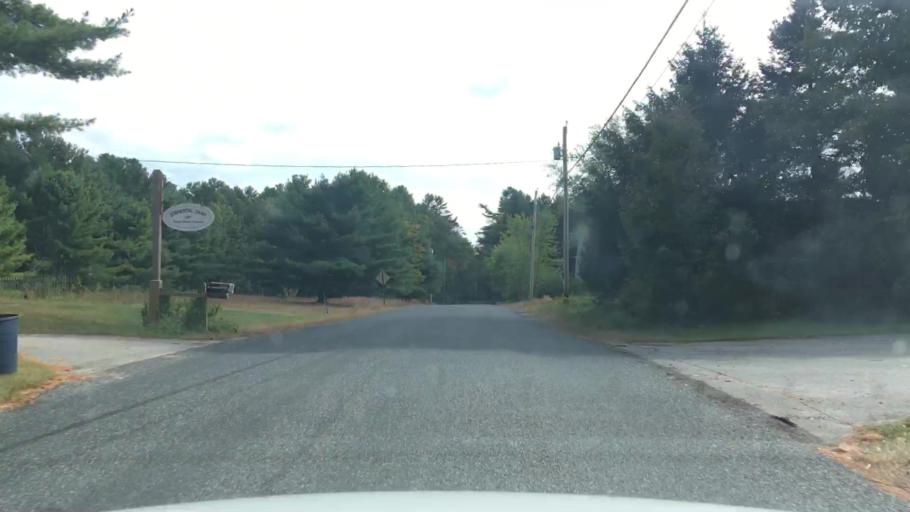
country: US
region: Maine
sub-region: Androscoggin County
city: Lisbon Falls
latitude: 43.9827
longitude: -70.0997
